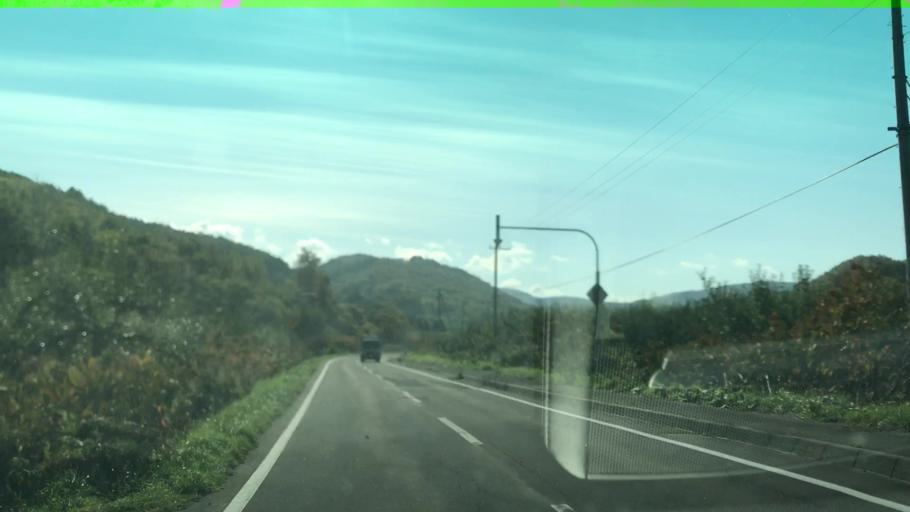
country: JP
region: Hokkaido
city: Yoichi
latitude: 43.1612
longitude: 140.8214
